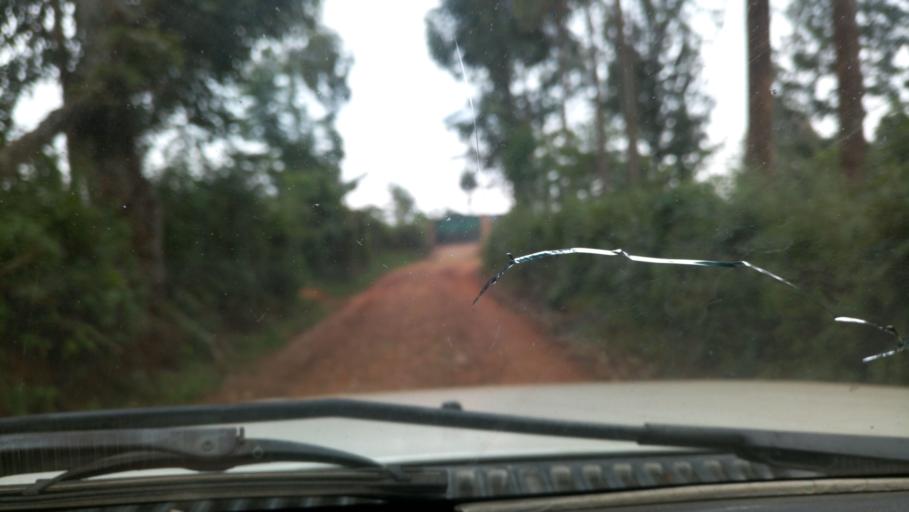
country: KE
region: Murang'a District
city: Kangema
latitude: -0.7441
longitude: 36.9353
